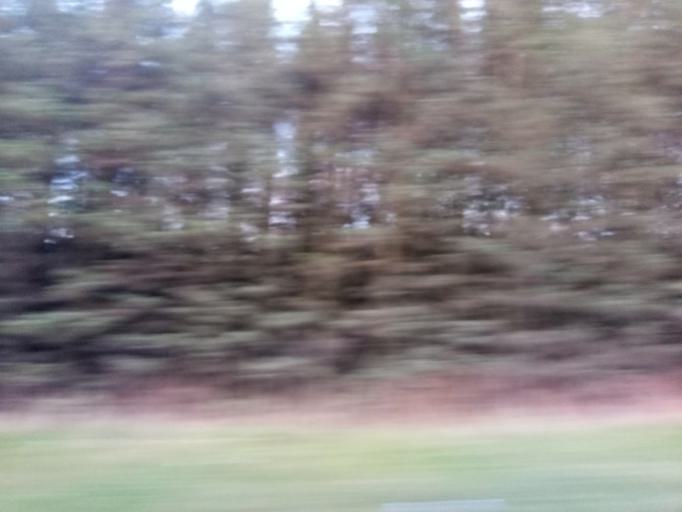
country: GB
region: Scotland
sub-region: East Lothian
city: Pencaitland
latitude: 55.8251
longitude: -2.8556
